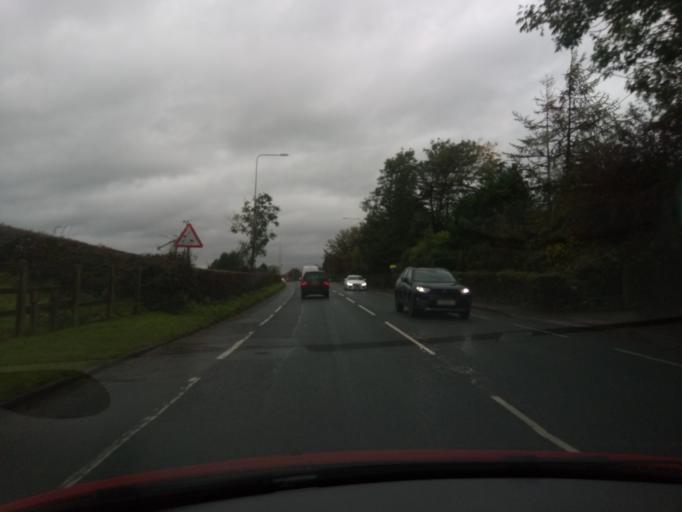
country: GB
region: England
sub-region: Lancashire
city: Preston
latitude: 53.8186
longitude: -2.7337
